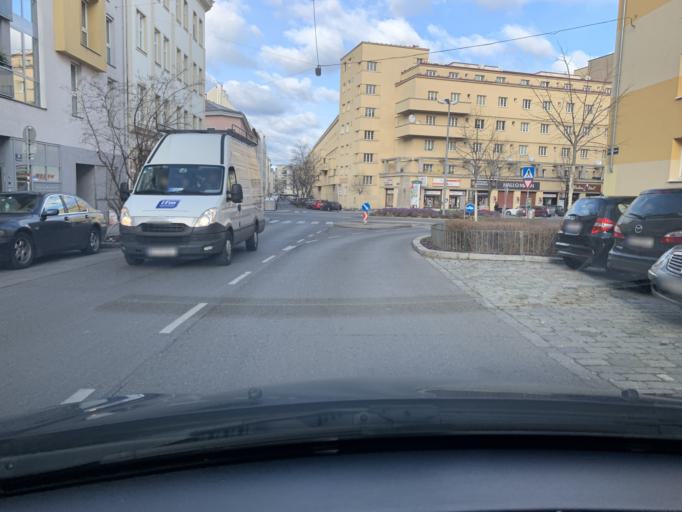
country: AT
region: Vienna
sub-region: Wien Stadt
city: Vienna
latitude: 48.1805
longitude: 16.3372
